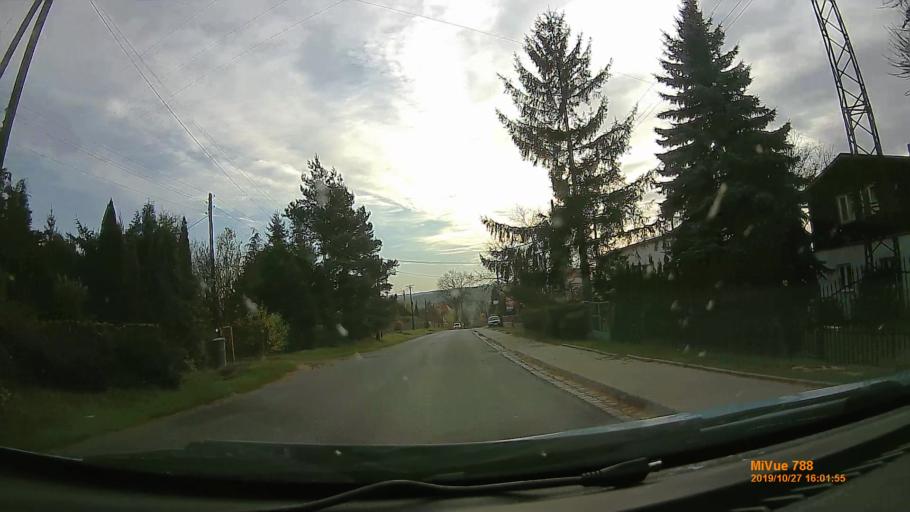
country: PL
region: Lower Silesian Voivodeship
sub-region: Powiat klodzki
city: Nowa Ruda
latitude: 50.5218
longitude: 16.5090
